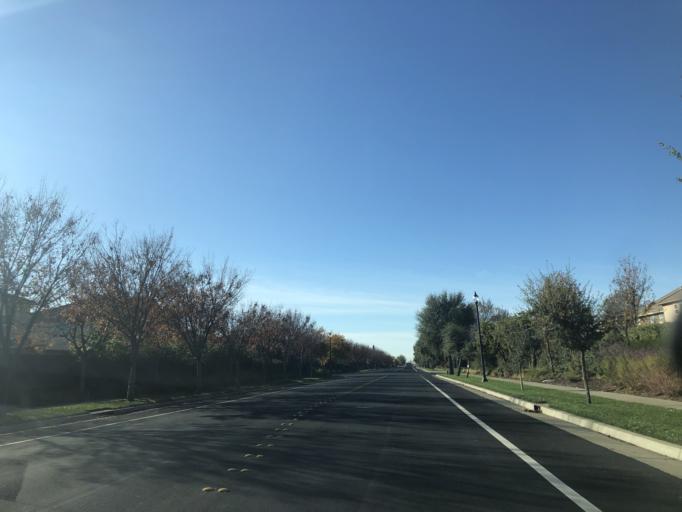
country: US
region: California
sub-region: Sacramento County
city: Antelope
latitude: 38.7808
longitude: -121.3714
